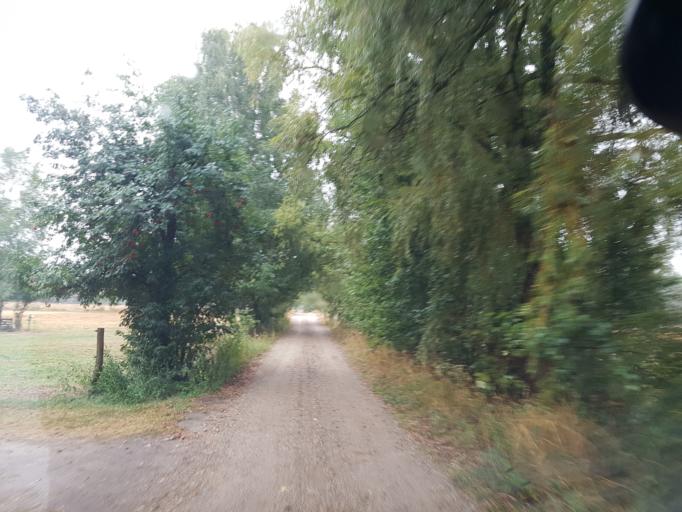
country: DE
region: Brandenburg
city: Finsterwalde
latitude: 51.6209
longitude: 13.7724
